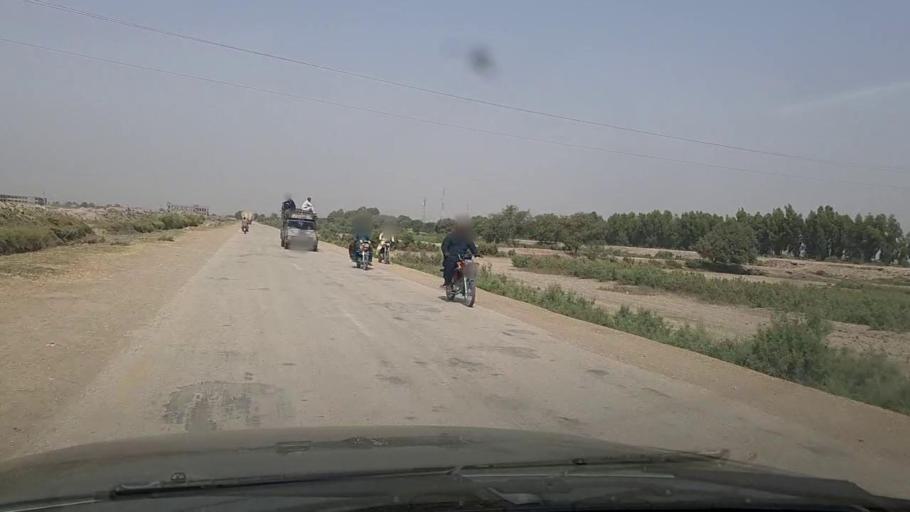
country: PK
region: Sindh
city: Thul
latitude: 28.3228
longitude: 68.7459
